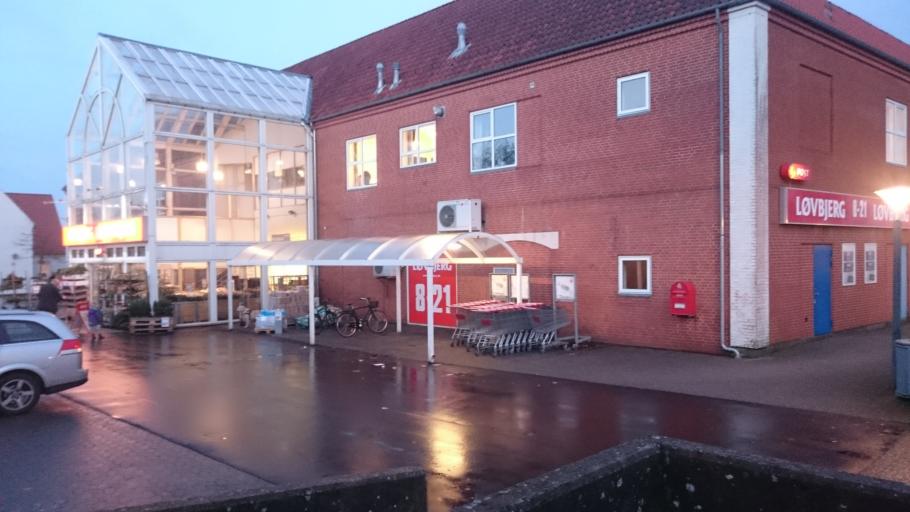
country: DK
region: South Denmark
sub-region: Vejen Kommune
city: Vejen
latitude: 55.4763
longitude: 9.1388
